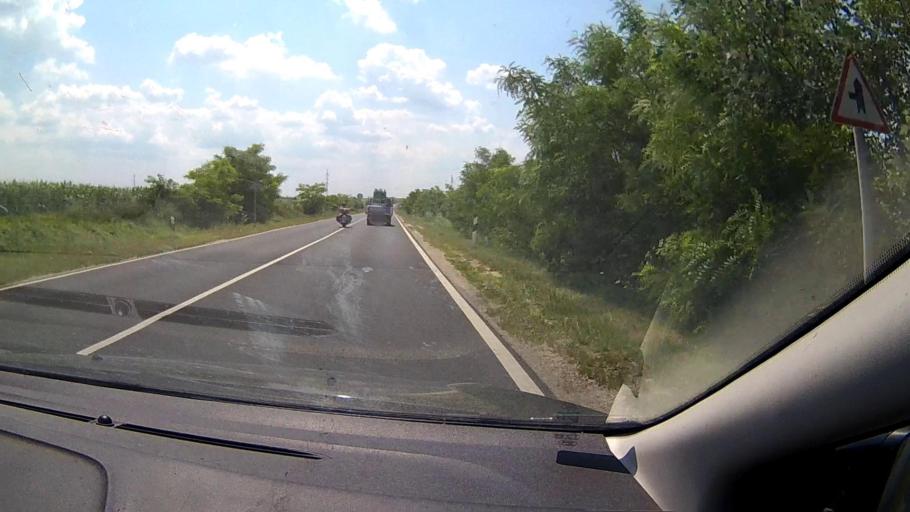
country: HU
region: Komarom-Esztergom
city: Tata
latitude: 47.6166
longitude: 18.3167
